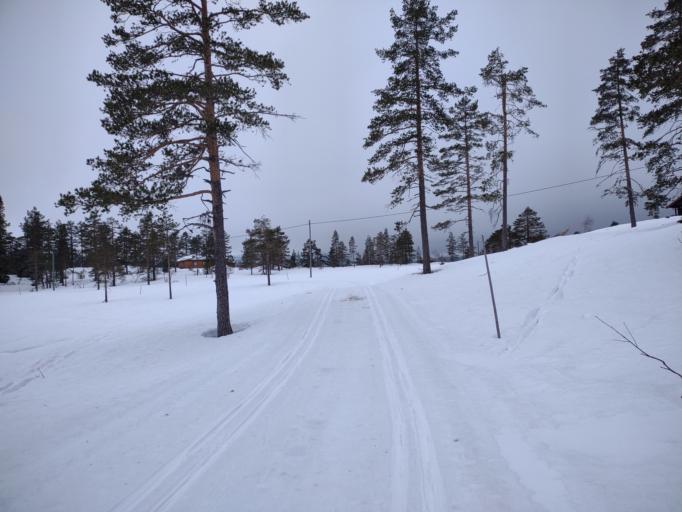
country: NO
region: Buskerud
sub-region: Flesberg
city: Lampeland
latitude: 59.7959
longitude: 9.4358
